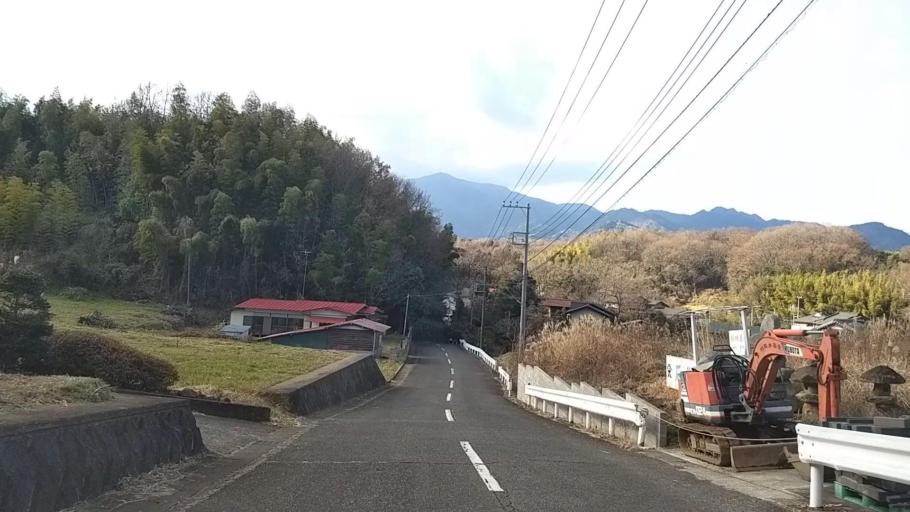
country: JP
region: Kanagawa
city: Isehara
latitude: 35.4301
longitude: 139.3130
